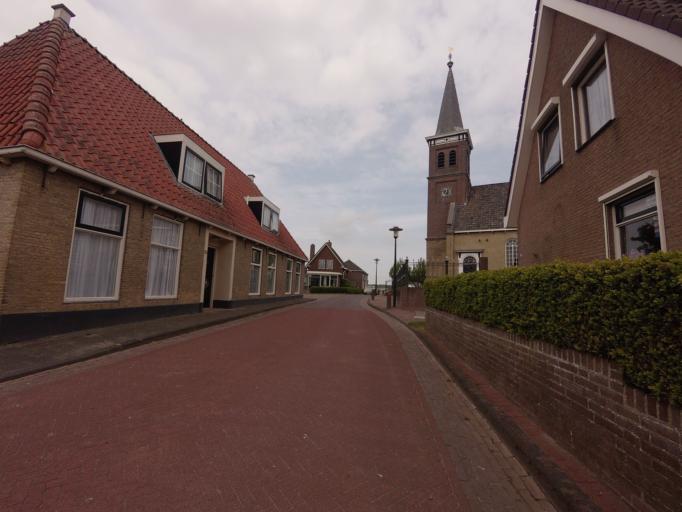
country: NL
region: Friesland
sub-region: Sudwest Fryslan
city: Bolsward
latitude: 53.0831
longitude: 5.4835
